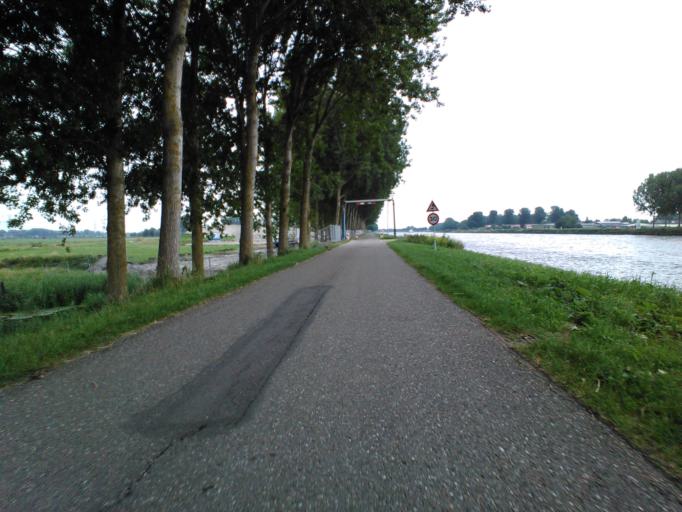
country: NL
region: North Holland
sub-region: Gemeente Amsterdam
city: Driemond
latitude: 52.2683
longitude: 5.0173
